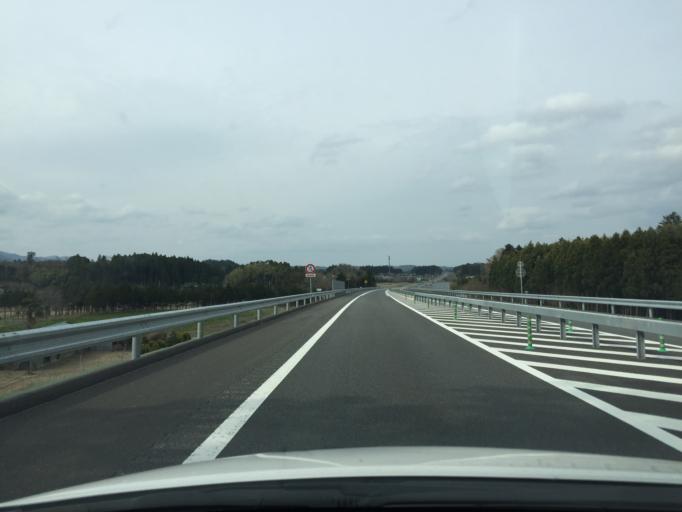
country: JP
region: Fukushima
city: Namie
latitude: 37.5381
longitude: 140.9410
